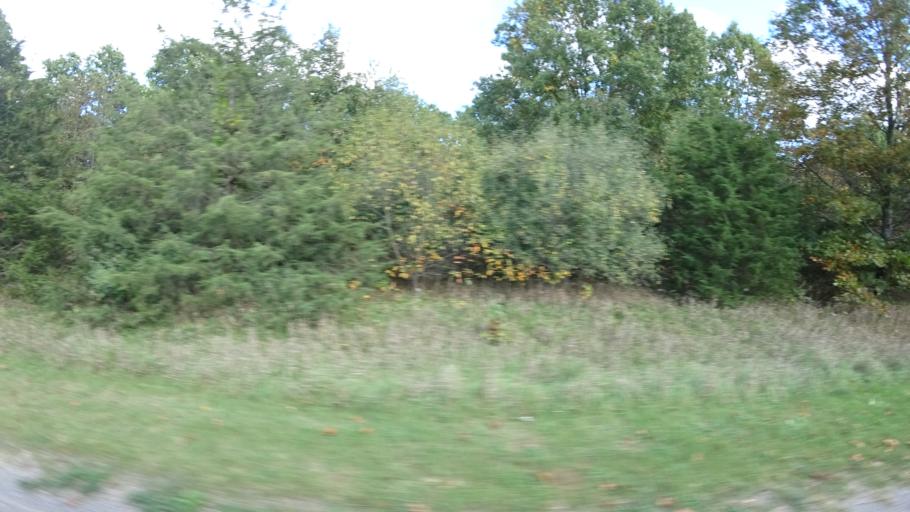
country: US
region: Michigan
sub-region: Saint Joseph County
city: Three Rivers
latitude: 41.9543
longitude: -85.5819
